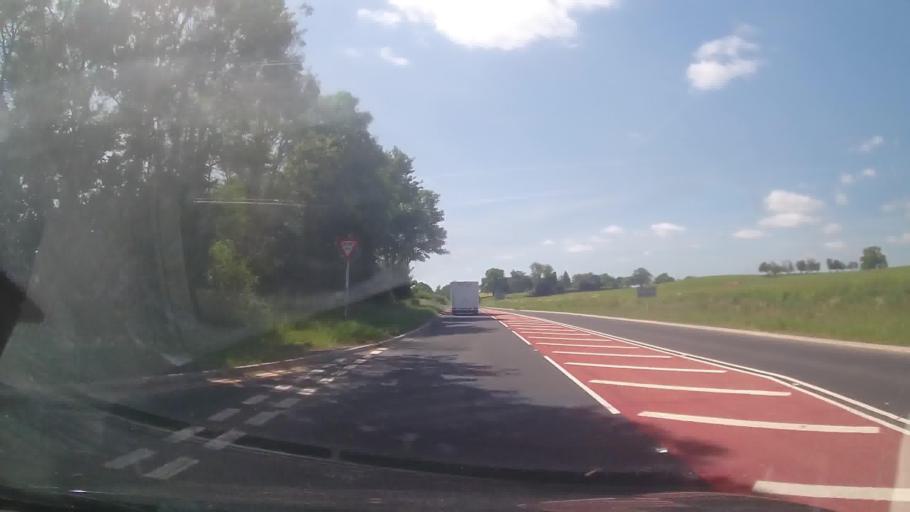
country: GB
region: England
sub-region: Shropshire
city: Ludlow
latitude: 52.3310
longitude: -2.7132
